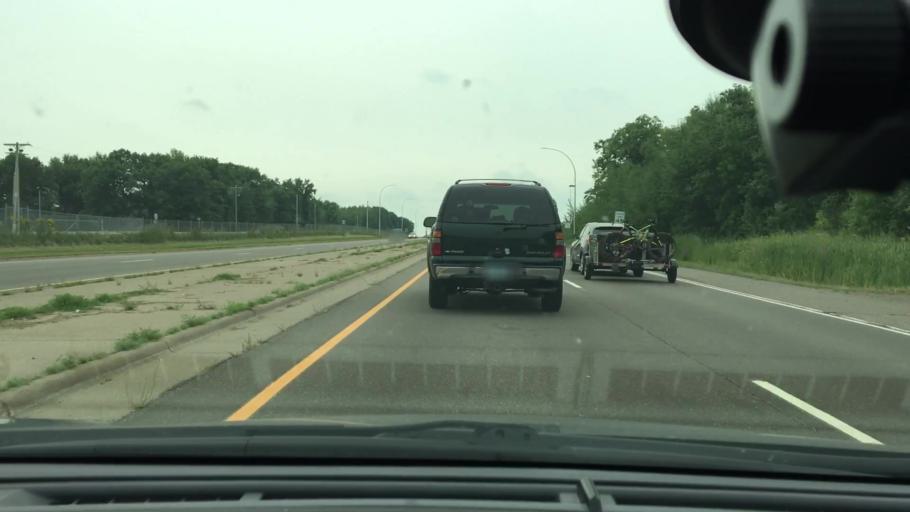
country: US
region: Minnesota
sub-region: Mille Lacs County
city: Vineland
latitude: 46.1838
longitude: -93.7566
